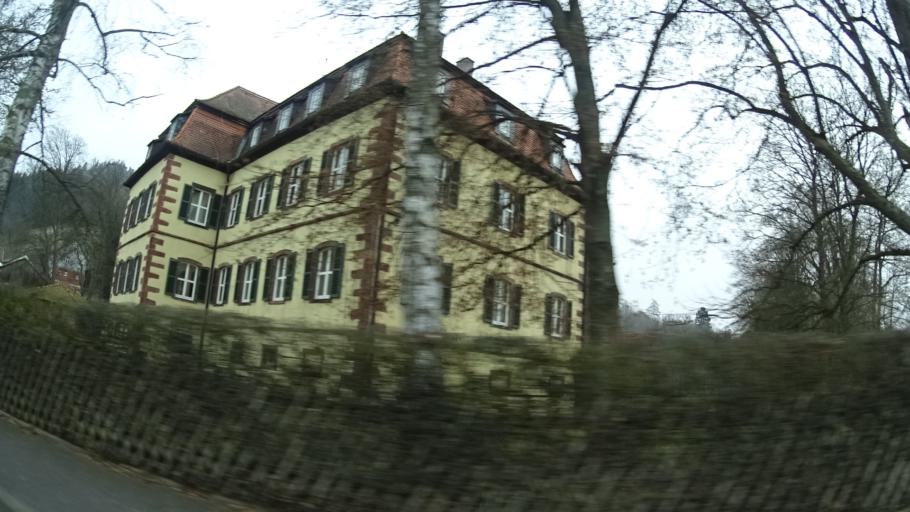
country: DE
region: Bavaria
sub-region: Regierungsbezirk Unterfranken
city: Zeitlofs
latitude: 50.2628
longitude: 9.6715
